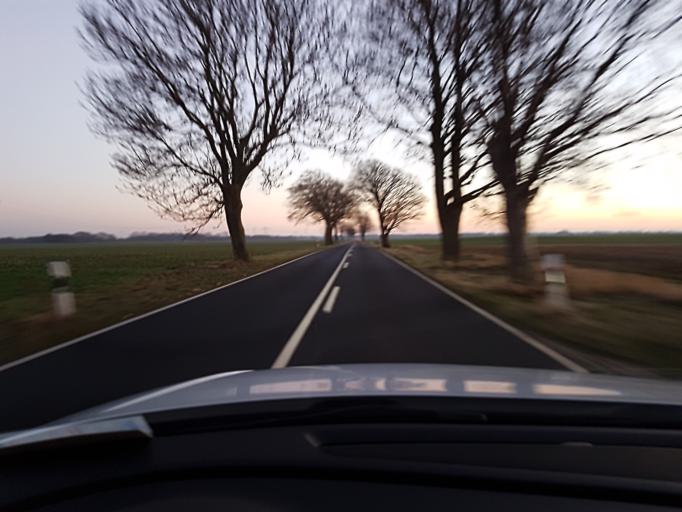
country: DE
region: Mecklenburg-Vorpommern
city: Gingst
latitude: 54.4967
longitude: 13.2817
